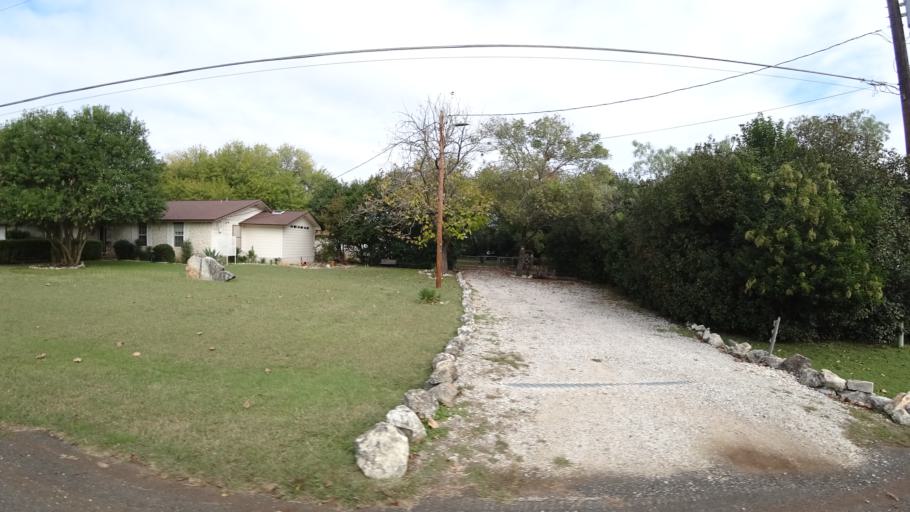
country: US
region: Texas
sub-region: Travis County
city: Manchaca
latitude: 30.1388
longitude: -97.8441
